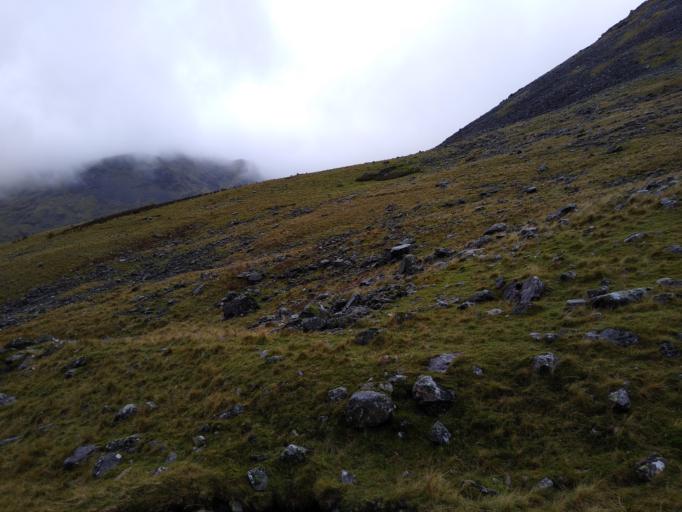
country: GB
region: England
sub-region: Cumbria
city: Keswick
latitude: 54.4893
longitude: -3.2582
